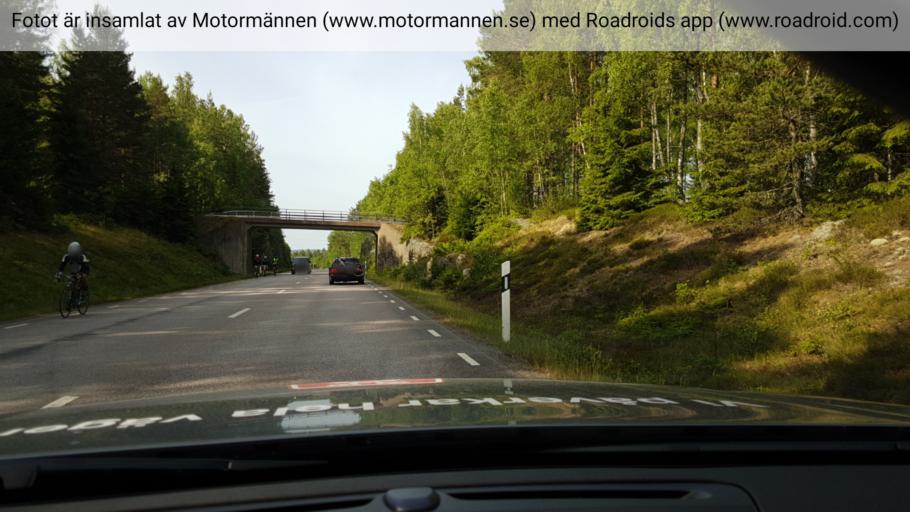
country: SE
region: Vaestra Goetaland
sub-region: Karlsborgs Kommun
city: Karlsborg
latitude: 58.5938
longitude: 14.5120
